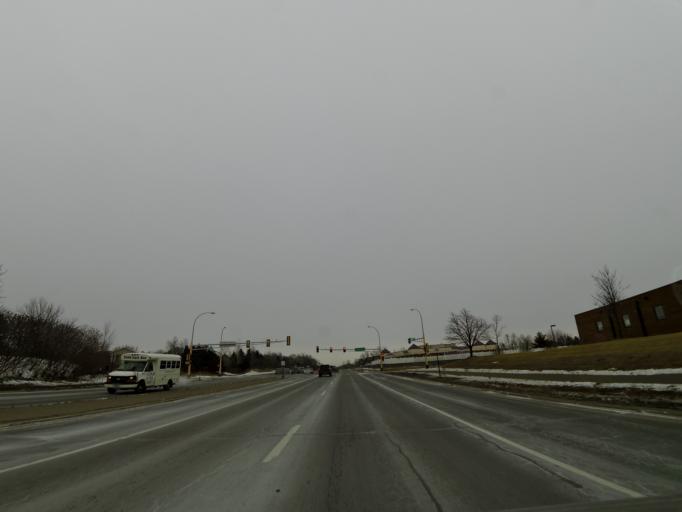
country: US
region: Minnesota
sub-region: Washington County
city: Woodbury
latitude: 44.9299
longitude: -92.9049
